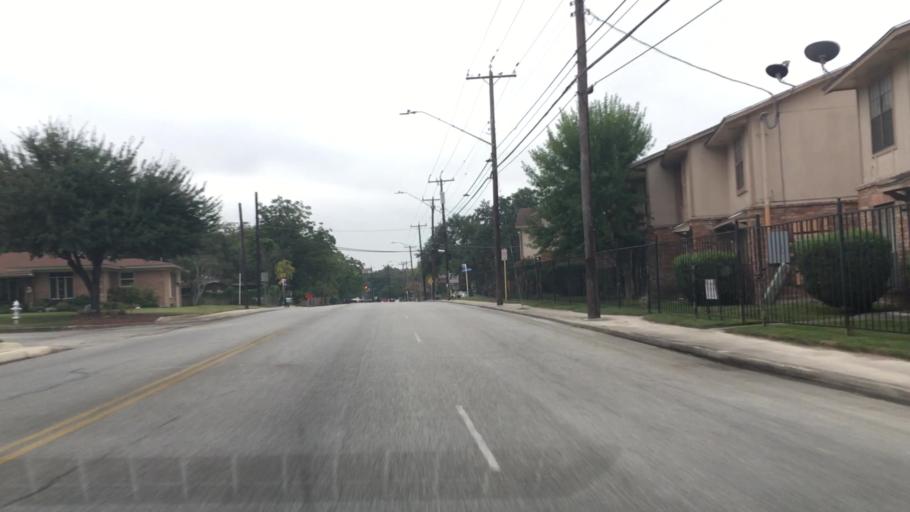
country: US
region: Texas
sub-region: Bexar County
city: Balcones Heights
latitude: 29.4812
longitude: -98.5540
